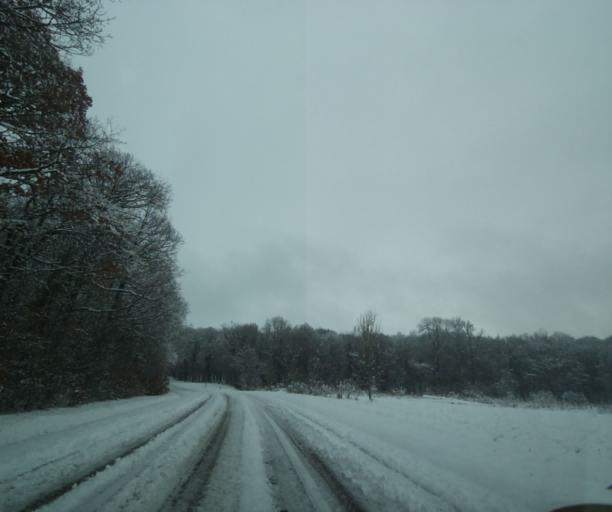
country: FR
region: Champagne-Ardenne
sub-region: Departement de la Haute-Marne
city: Montier-en-Der
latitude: 48.5442
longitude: 4.8006
